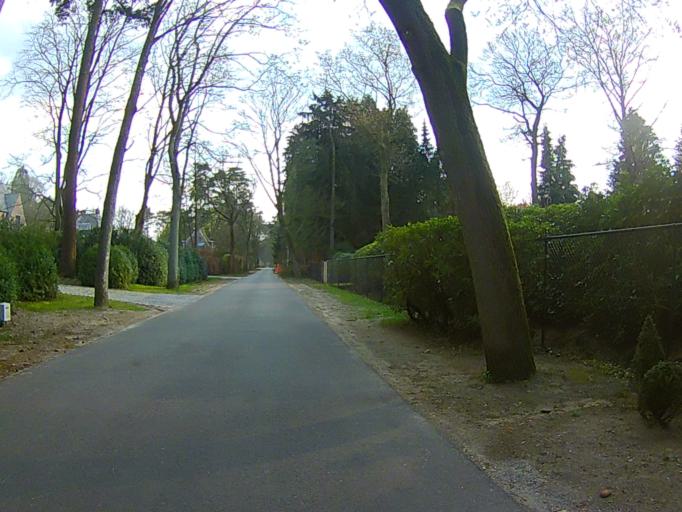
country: BE
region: Flanders
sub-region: Provincie Antwerpen
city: Kalmthout
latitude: 51.3495
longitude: 4.4618
